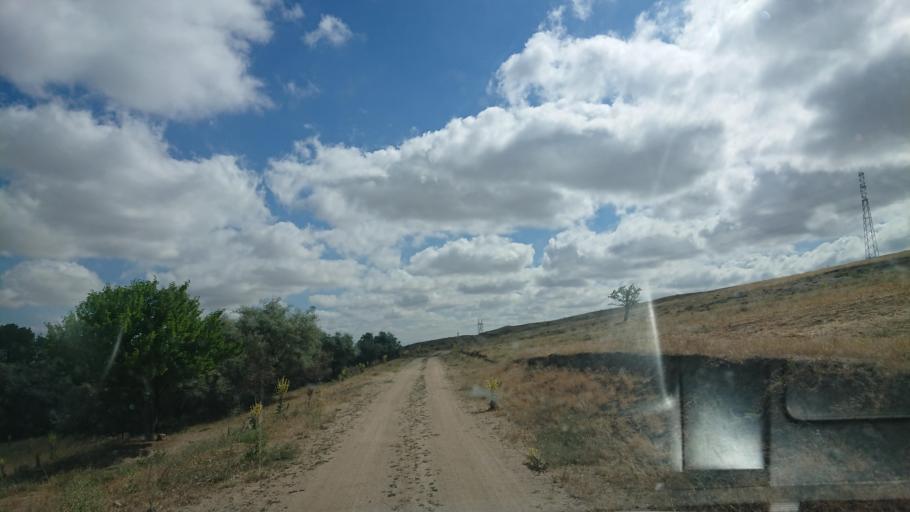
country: TR
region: Aksaray
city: Agacoren
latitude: 38.8561
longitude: 33.9385
